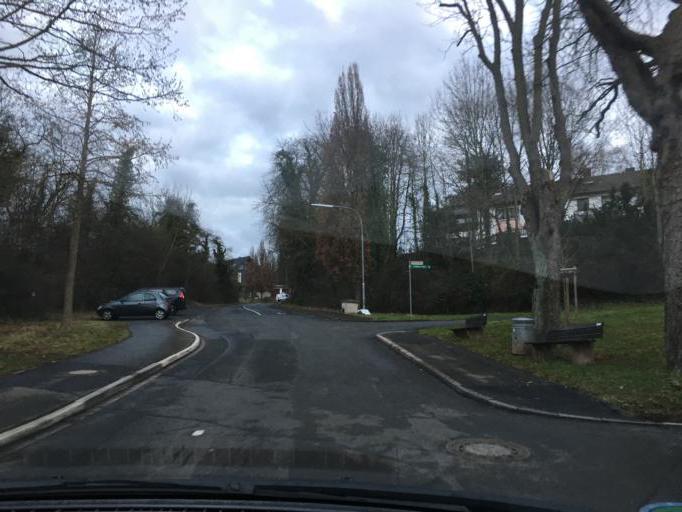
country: DE
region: North Rhine-Westphalia
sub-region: Regierungsbezirk Koln
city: Mechernich
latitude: 50.6091
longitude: 6.6472
